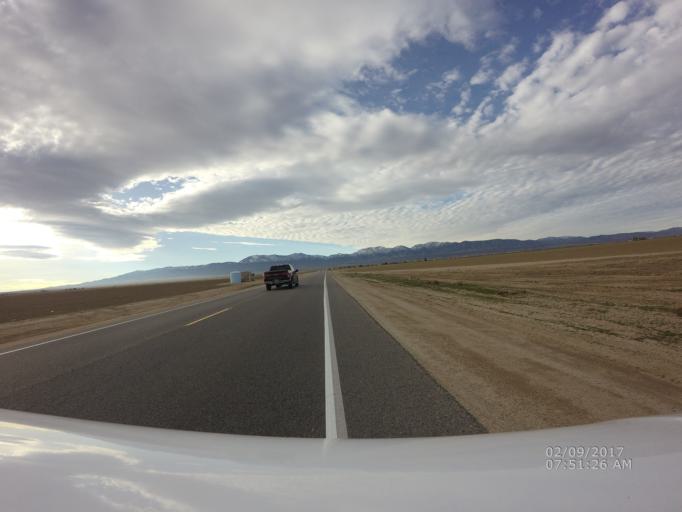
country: US
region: California
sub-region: Los Angeles County
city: Lake Los Angeles
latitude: 34.5704
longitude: -117.8266
